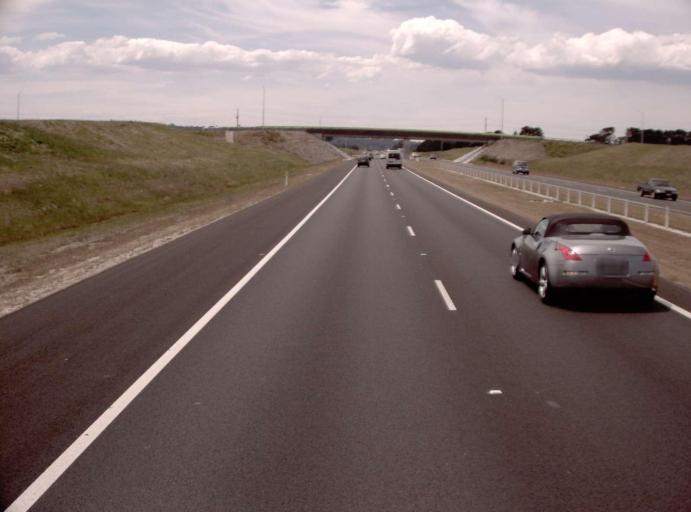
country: AU
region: Victoria
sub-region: Mornington Peninsula
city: Moorooduc
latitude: -38.2352
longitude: 145.1245
